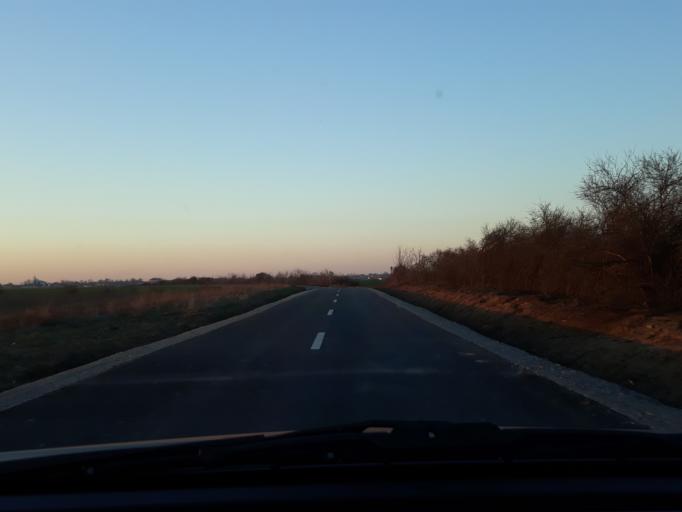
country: RO
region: Bihor
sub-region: Comuna Gepiu
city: Gepiu
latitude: 46.9154
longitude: 21.7876
